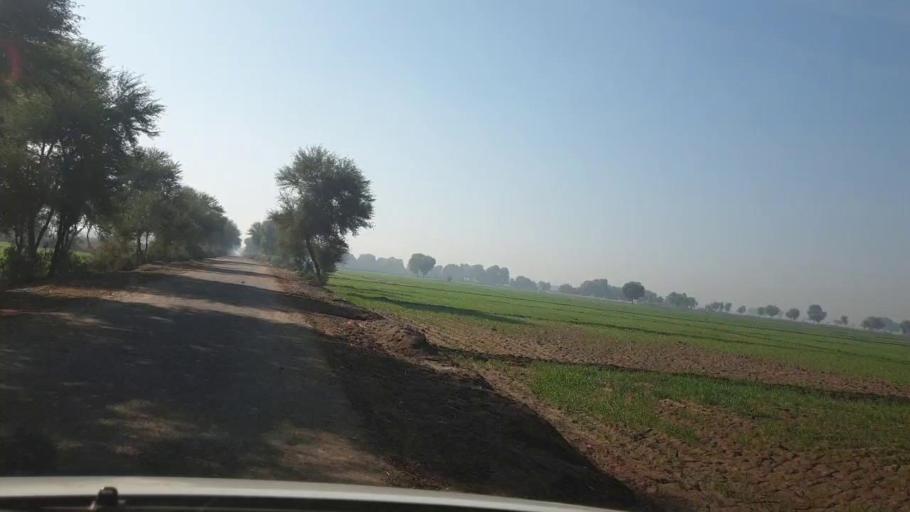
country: PK
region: Sindh
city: Dadu
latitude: 26.6446
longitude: 67.8213
